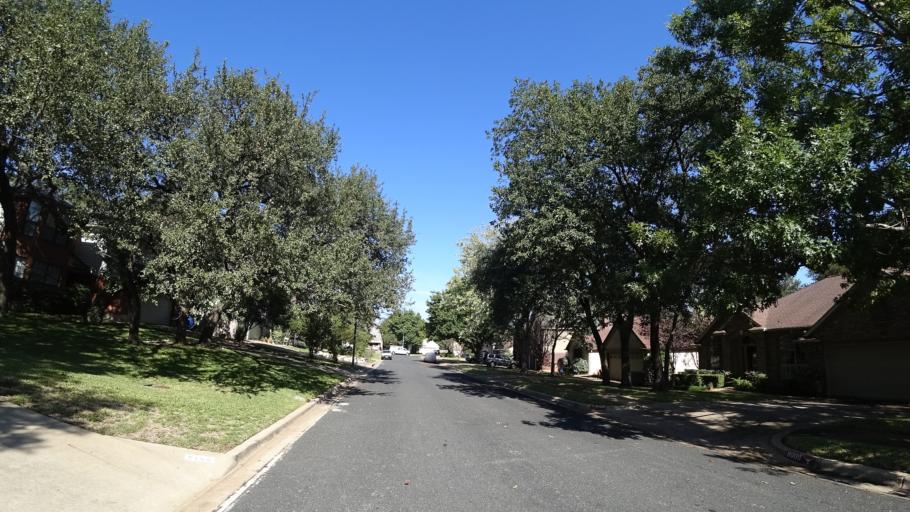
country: US
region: Texas
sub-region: Travis County
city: Shady Hollow
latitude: 30.2171
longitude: -97.8699
